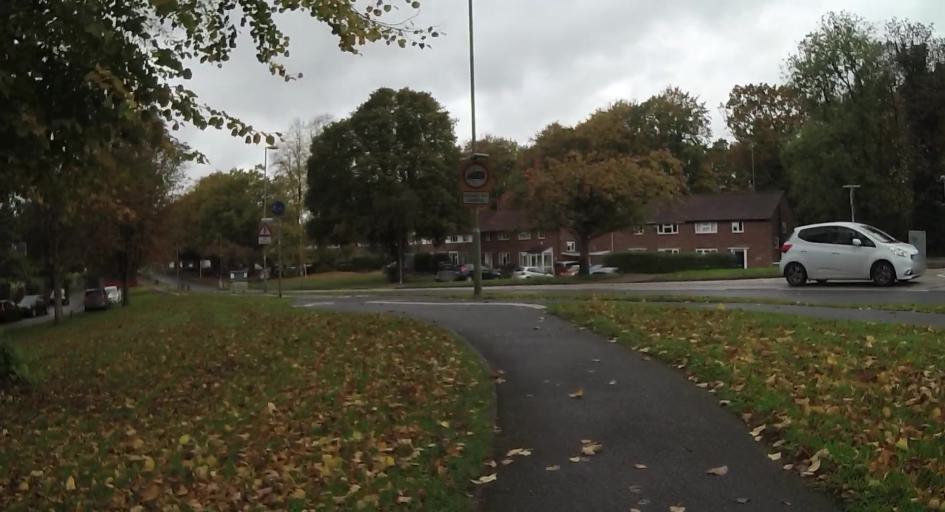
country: GB
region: England
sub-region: Surrey
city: West Byfleet
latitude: 51.3380
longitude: -0.5169
